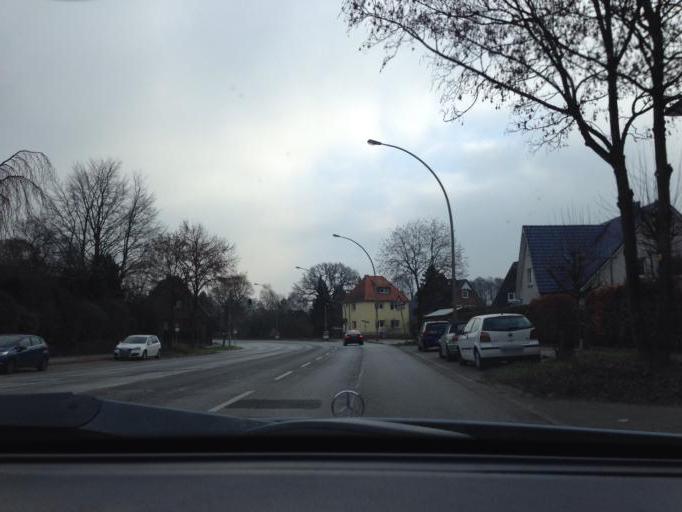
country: DE
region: Hamburg
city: Farmsen-Berne
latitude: 53.6139
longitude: 10.1585
